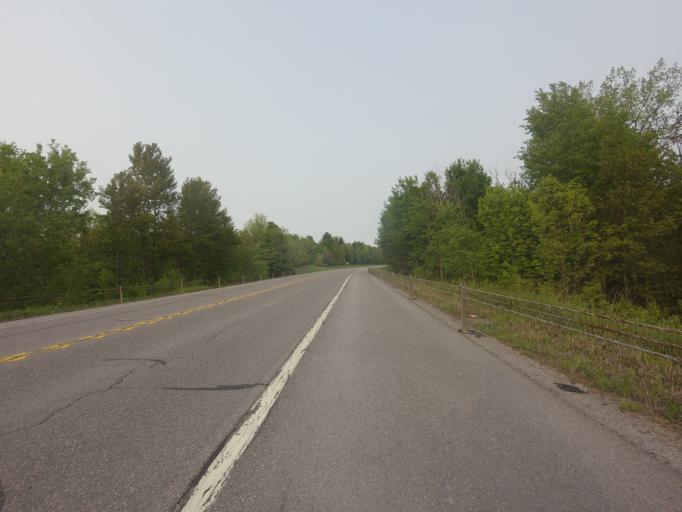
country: US
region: New York
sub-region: St. Lawrence County
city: Gouverneur
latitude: 44.1189
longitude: -75.3841
